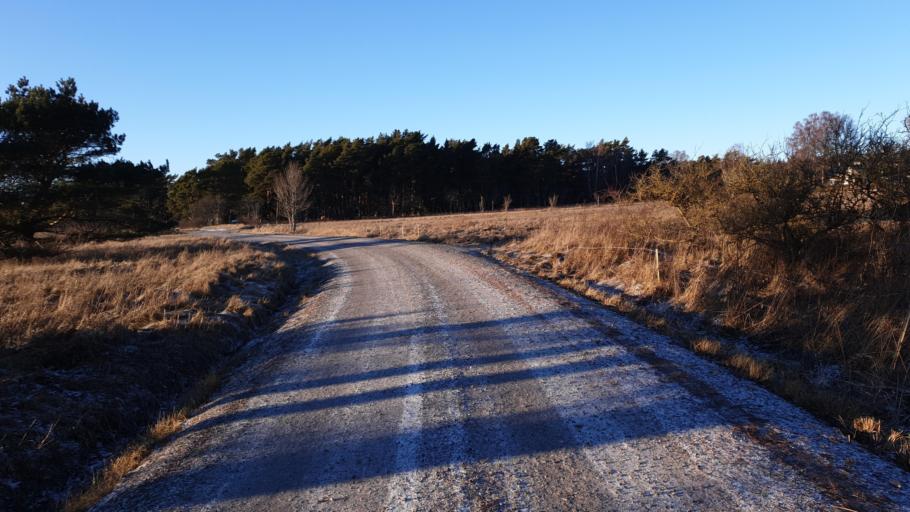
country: SE
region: Gotland
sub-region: Gotland
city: Slite
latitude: 57.3741
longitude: 18.8036
